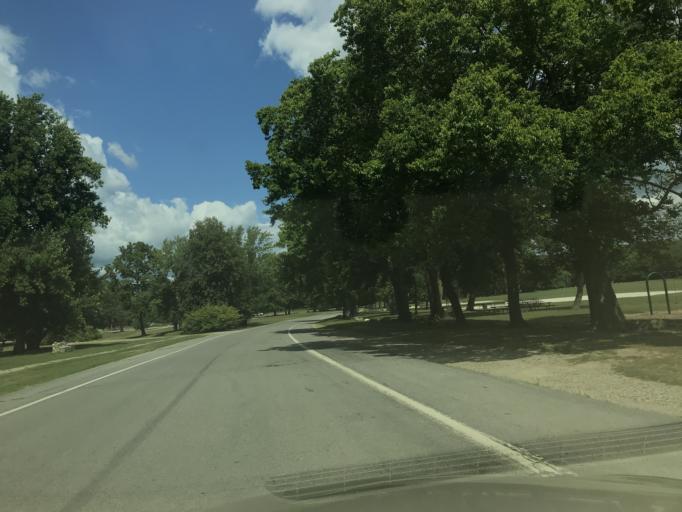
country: US
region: Michigan
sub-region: Jackson County
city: Vandercook Lake
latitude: 42.2150
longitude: -84.4157
